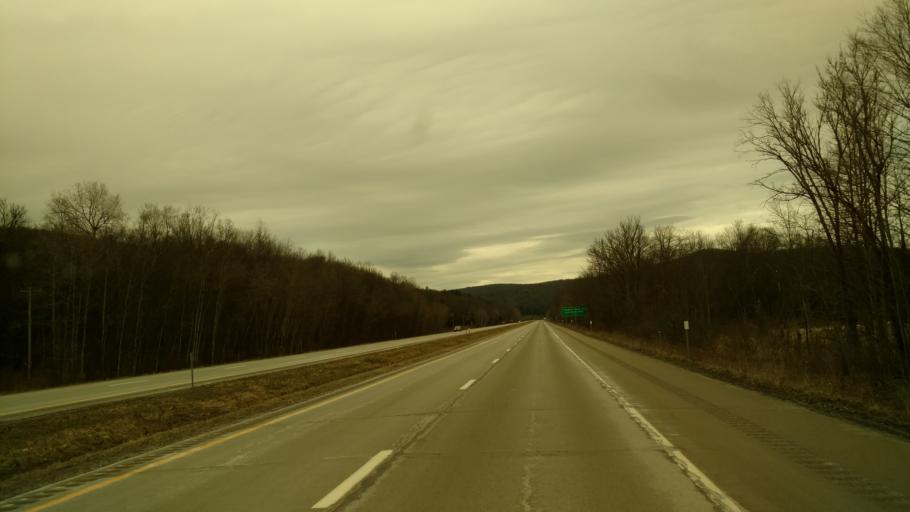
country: US
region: New York
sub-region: Cattaraugus County
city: Salamanca
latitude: 42.1254
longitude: -78.7791
